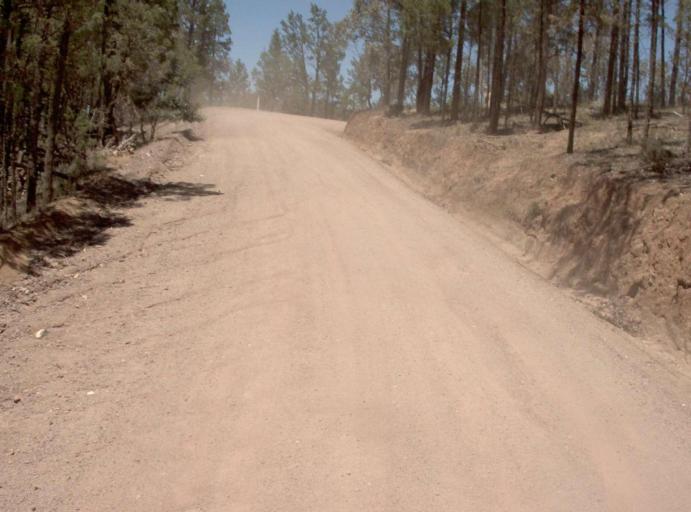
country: AU
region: New South Wales
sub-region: Snowy River
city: Jindabyne
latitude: -36.9282
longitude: 148.3853
